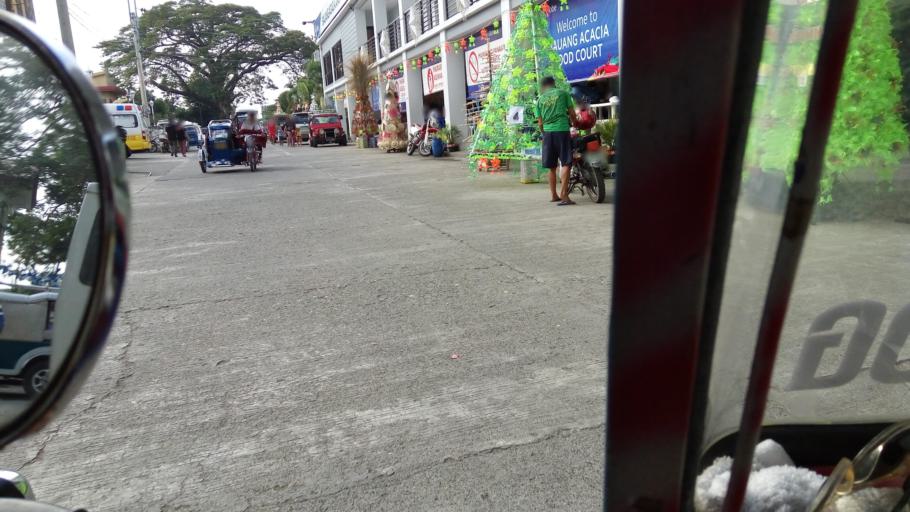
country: PH
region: Ilocos
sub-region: Province of La Union
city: Bauang
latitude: 16.5268
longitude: 120.3306
